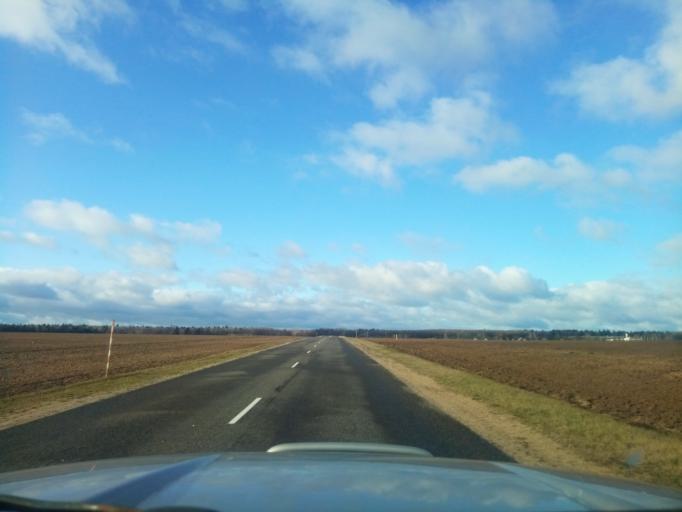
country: BY
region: Minsk
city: Kapyl'
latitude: 53.1698
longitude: 27.0455
